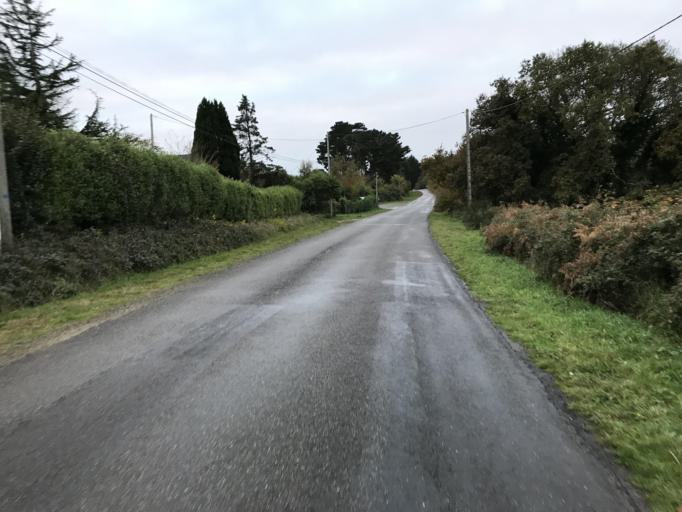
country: FR
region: Brittany
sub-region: Departement du Finistere
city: Logonna-Daoulas
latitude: 48.3173
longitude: -4.3269
